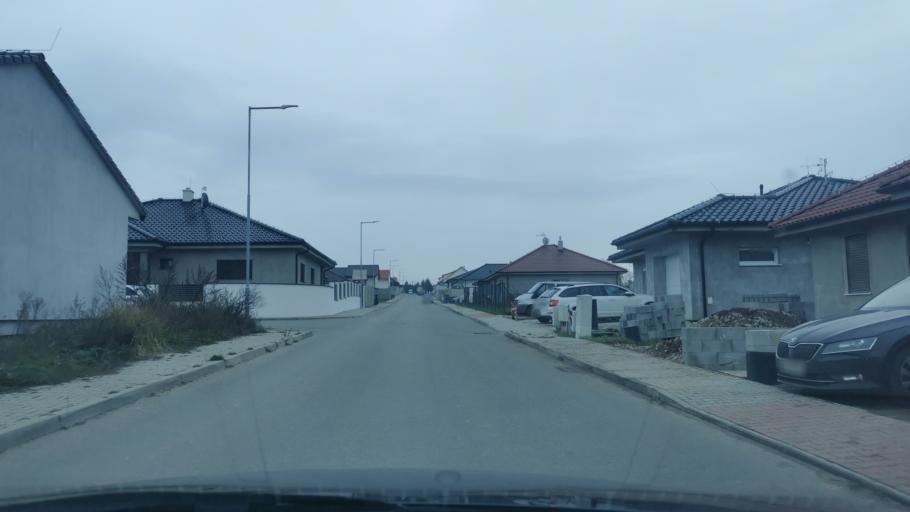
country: SK
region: Trnavsky
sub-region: Okres Skalica
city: Holic
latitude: 48.8186
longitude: 17.1673
